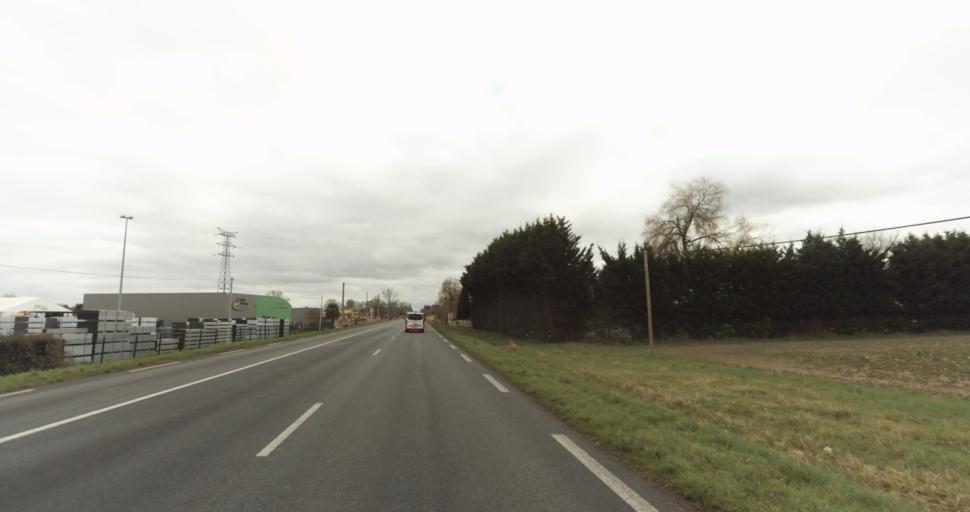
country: FR
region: Pays de la Loire
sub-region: Departement de Maine-et-Loire
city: Vivy
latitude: 47.3669
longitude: -0.0953
